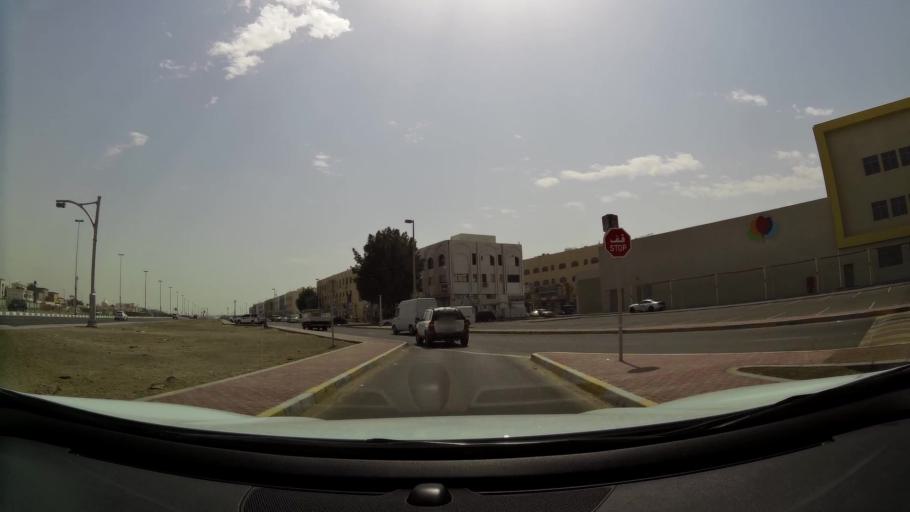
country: AE
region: Abu Dhabi
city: Abu Dhabi
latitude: 24.2986
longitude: 54.6370
